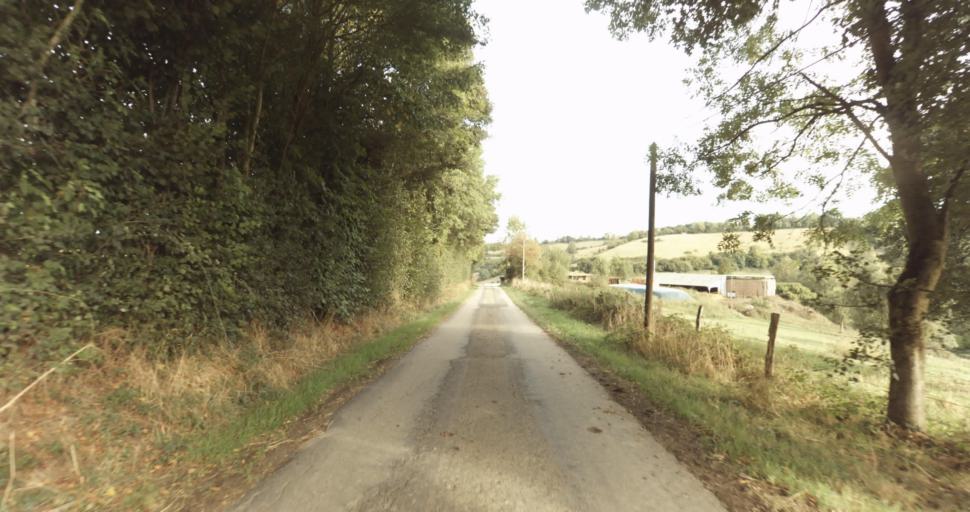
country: FR
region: Lower Normandy
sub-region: Departement de l'Orne
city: Vimoutiers
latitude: 48.8685
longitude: 0.2446
